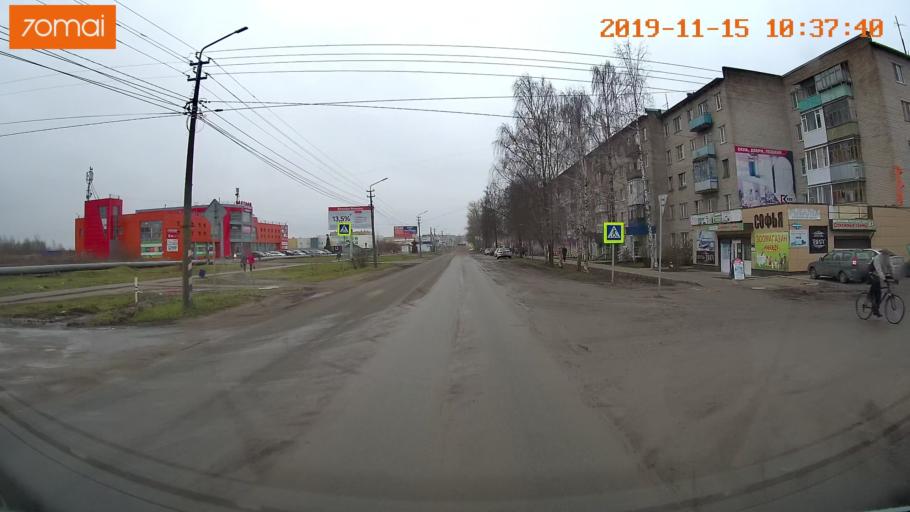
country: RU
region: Vologda
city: Sheksna
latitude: 59.2316
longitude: 38.5129
